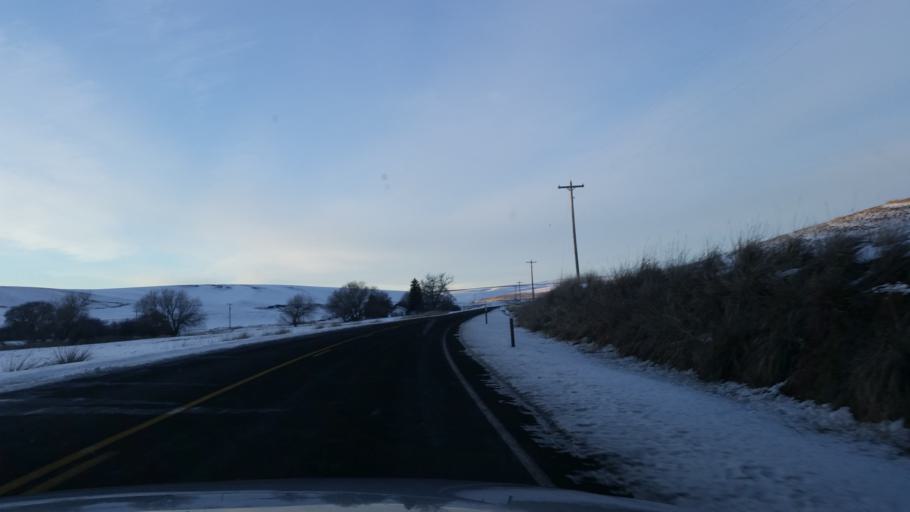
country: US
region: Washington
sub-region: Whitman County
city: Colfax
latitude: 47.1066
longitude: -117.6316
